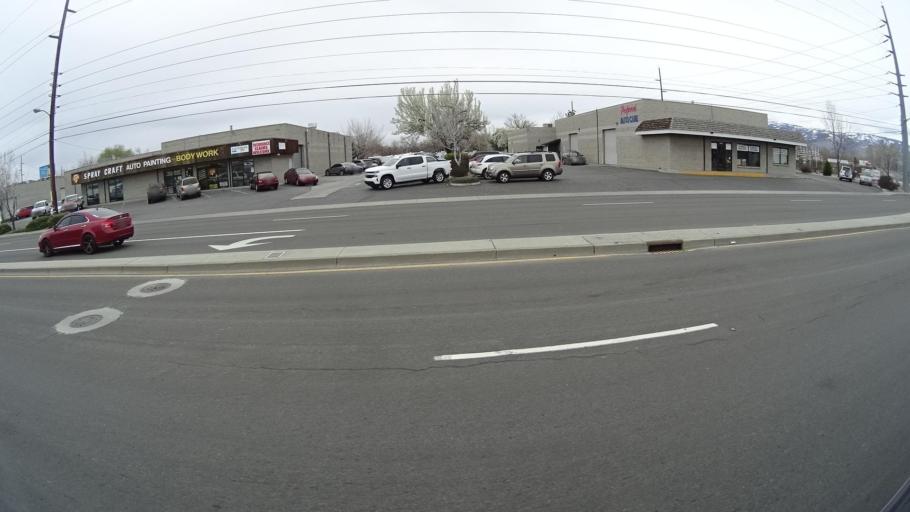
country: US
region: Nevada
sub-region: Washoe County
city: Sparks
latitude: 39.5235
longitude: -119.7681
